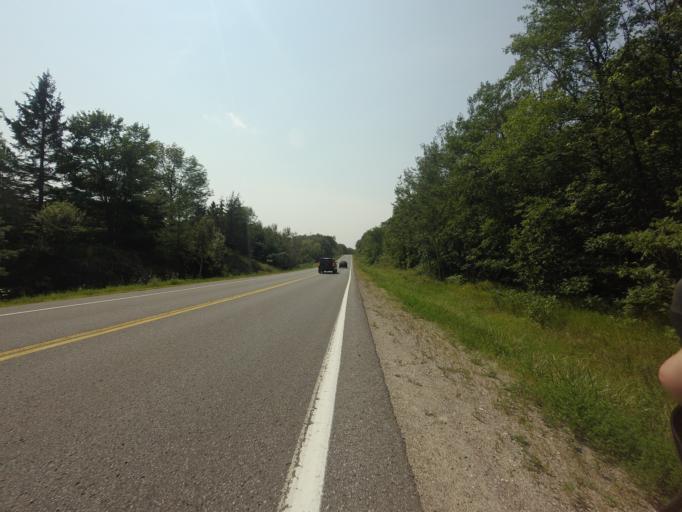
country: CA
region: Ontario
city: Skatepark
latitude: 44.6585
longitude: -76.7001
